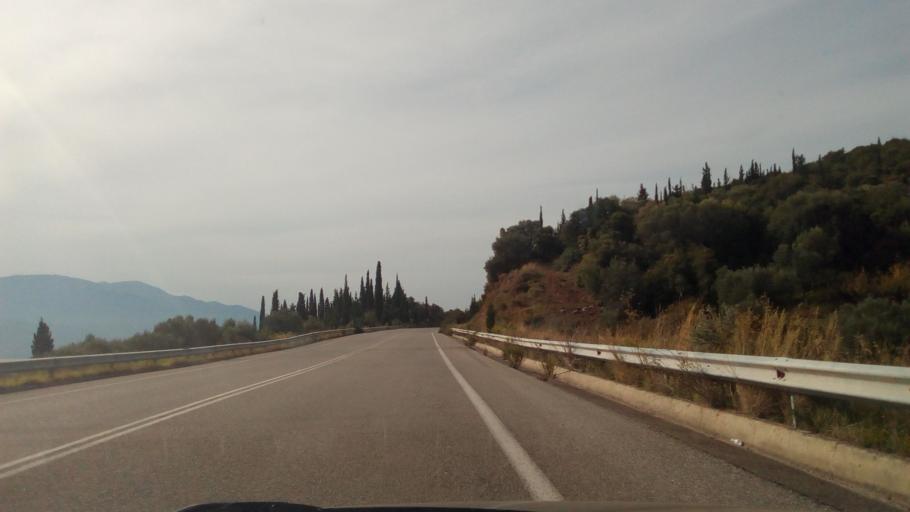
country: GR
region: West Greece
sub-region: Nomos Aitolias kai Akarnanias
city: Nafpaktos
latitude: 38.3880
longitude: 21.7965
